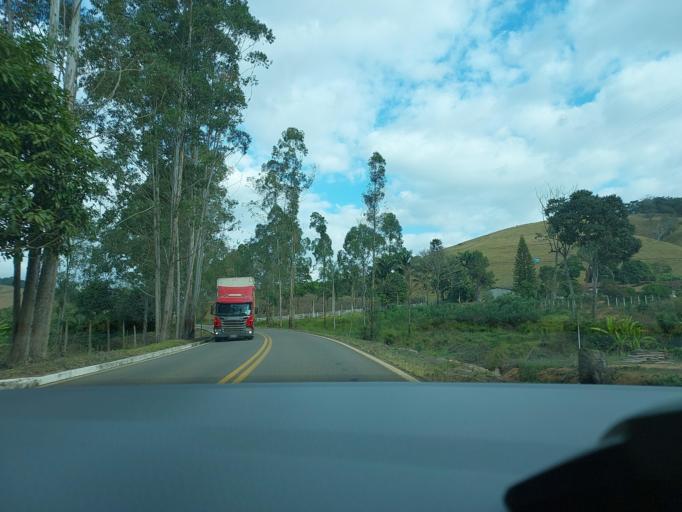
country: BR
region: Minas Gerais
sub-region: Visconde Do Rio Branco
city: Visconde do Rio Branco
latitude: -20.9214
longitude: -42.6383
